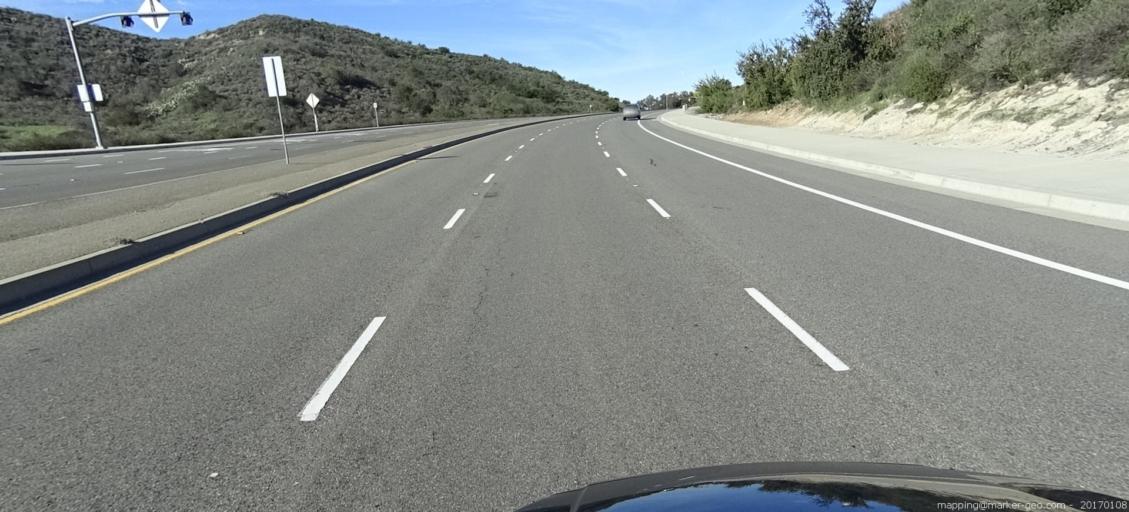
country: US
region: California
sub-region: Orange County
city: Las Flores
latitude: 33.5859
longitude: -117.6149
